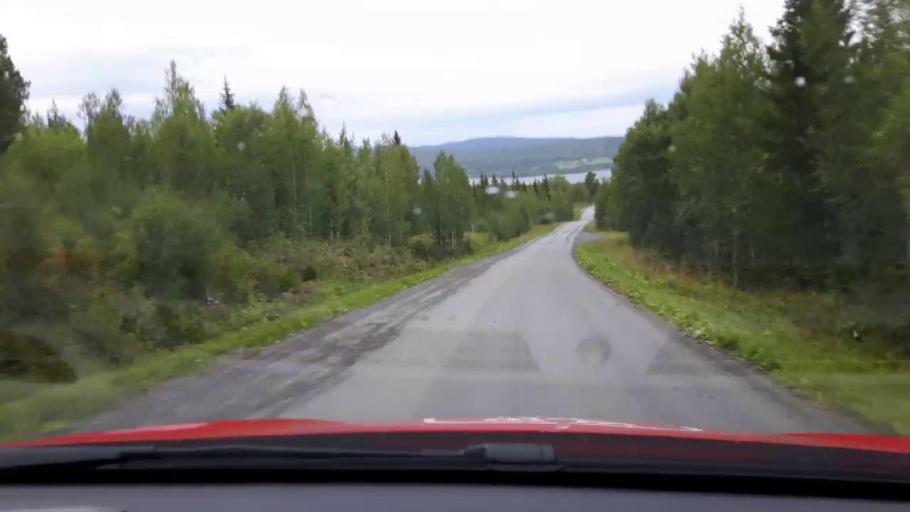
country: SE
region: Jaemtland
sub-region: Are Kommun
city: Are
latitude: 63.4366
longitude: 13.2108
